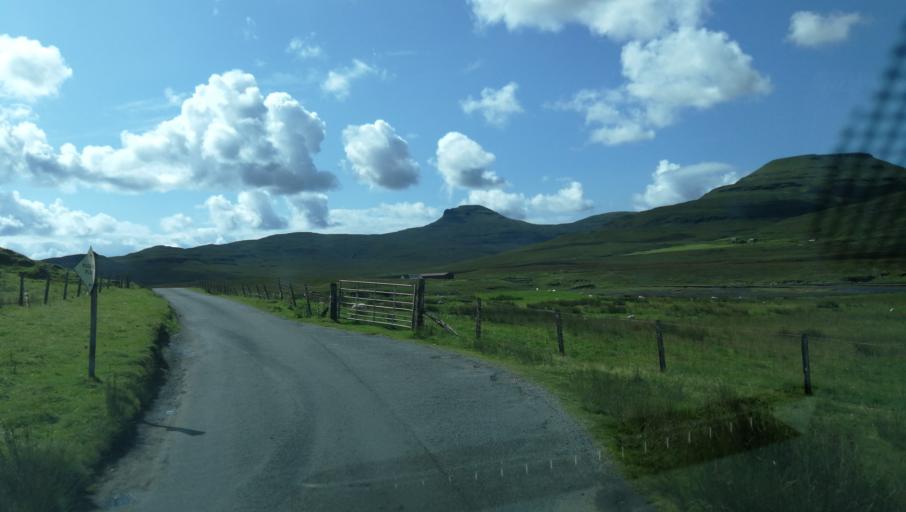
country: GB
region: Scotland
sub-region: Highland
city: Isle of Skye
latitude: 57.4253
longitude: -6.5801
